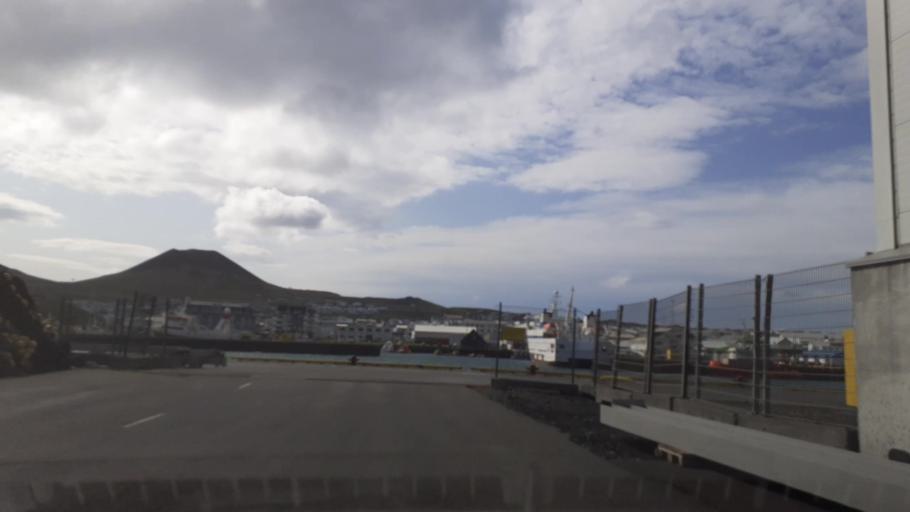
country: IS
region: South
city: Vestmannaeyjar
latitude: 63.4464
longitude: -20.2708
